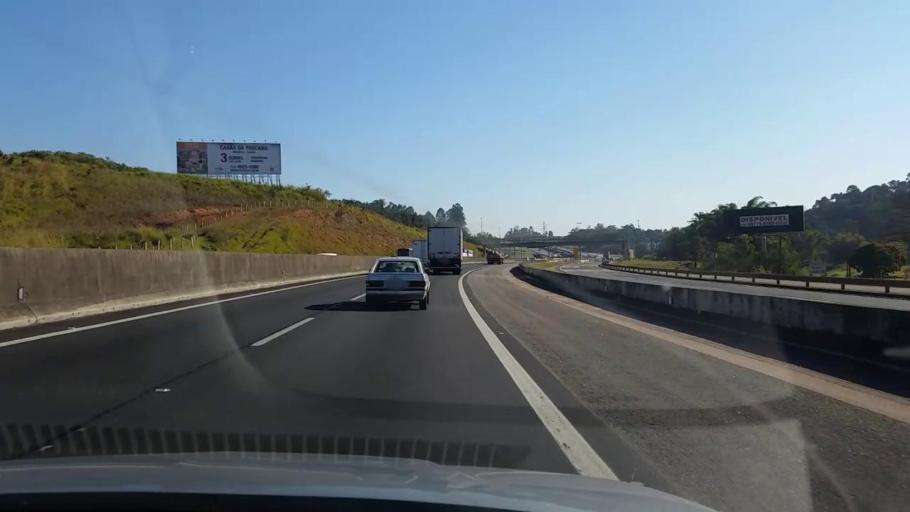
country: BR
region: Sao Paulo
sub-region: Varzea Paulista
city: Varzea Paulista
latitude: -23.2435
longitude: -46.8683
